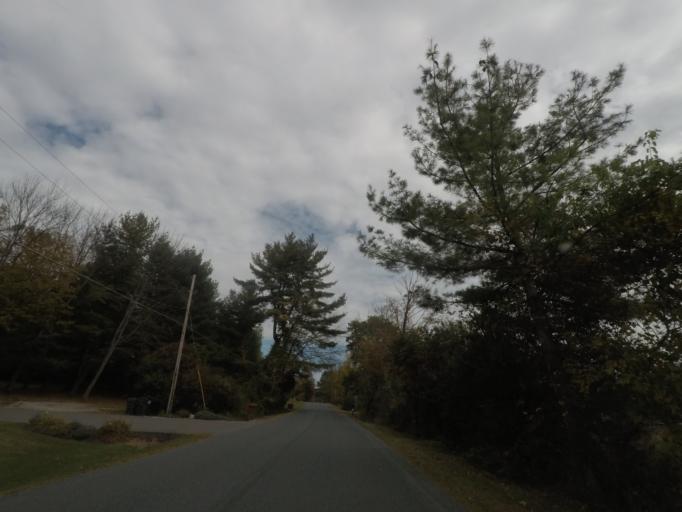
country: US
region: New York
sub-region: Rensselaer County
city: Nassau
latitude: 42.5526
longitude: -73.6485
